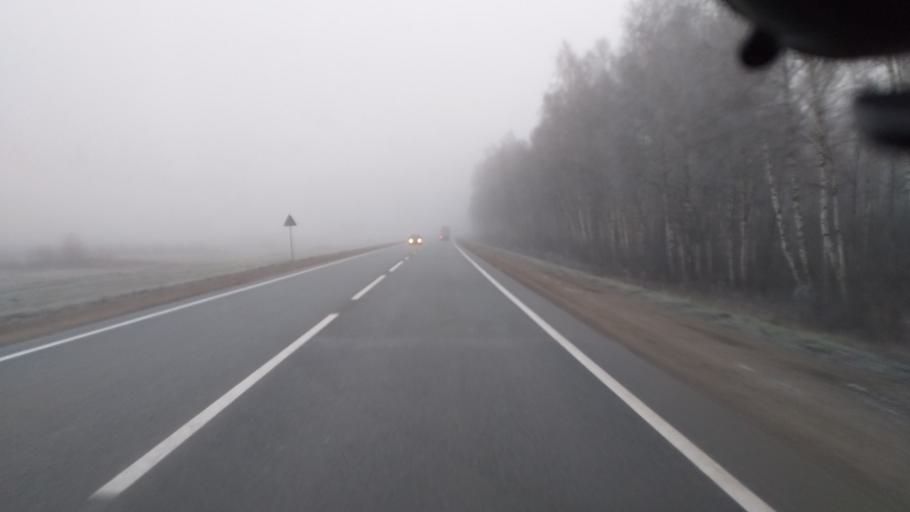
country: LV
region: Marupe
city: Marupe
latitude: 56.8549
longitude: 23.9997
